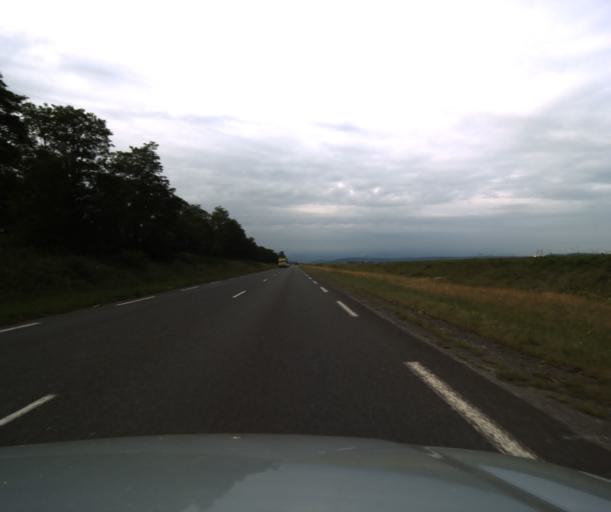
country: FR
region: Midi-Pyrenees
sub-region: Departement des Hautes-Pyrenees
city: Juillan
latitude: 43.2138
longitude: 0.0140
